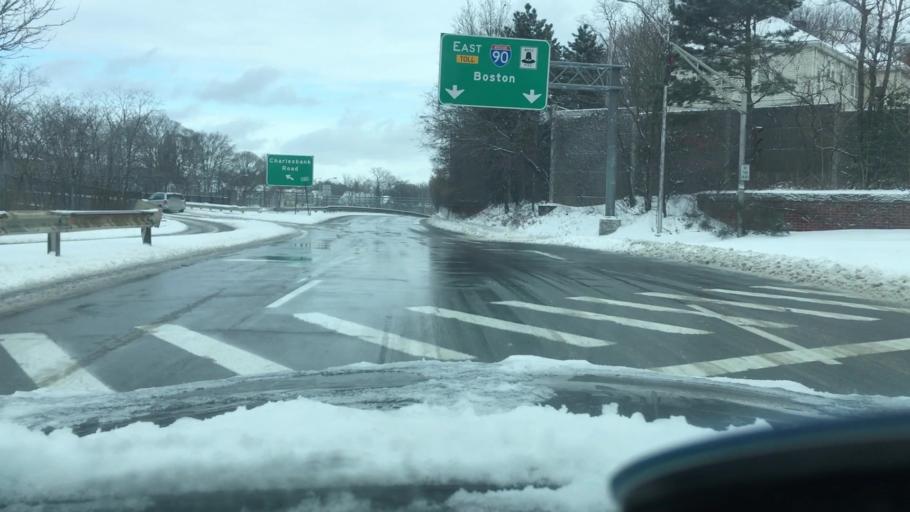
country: US
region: Massachusetts
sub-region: Middlesex County
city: Watertown
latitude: 42.3567
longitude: -71.1820
